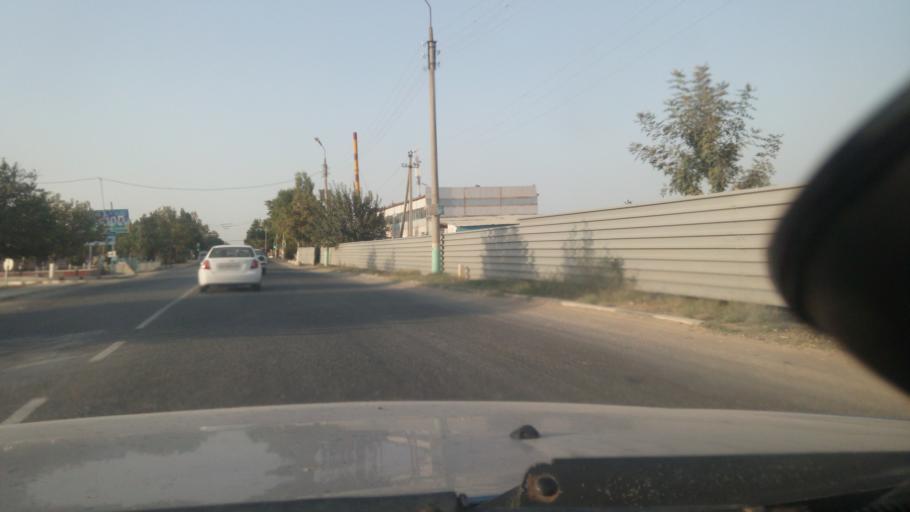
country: UZ
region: Sirdaryo
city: Guliston
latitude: 40.4764
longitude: 68.7763
